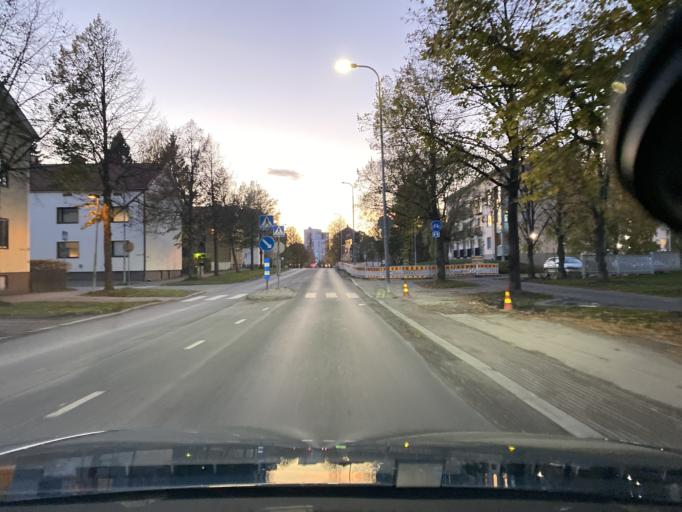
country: FI
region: Pirkanmaa
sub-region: Tampere
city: Tampere
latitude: 61.4706
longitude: 23.7316
